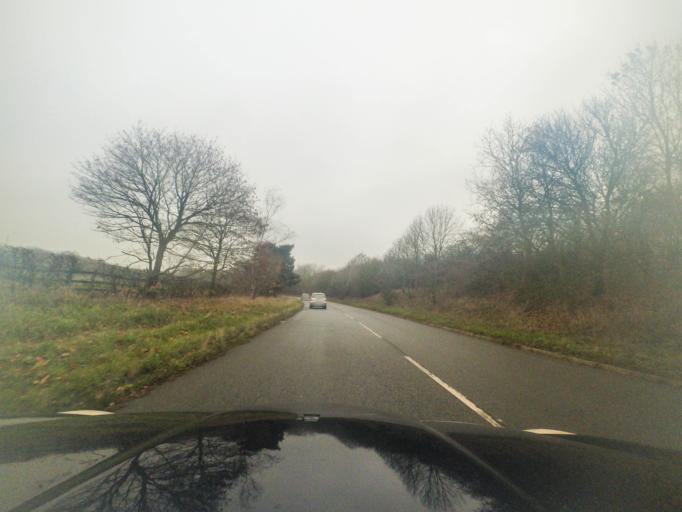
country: GB
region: England
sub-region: Solihull
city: Barston
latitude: 52.3929
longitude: -1.6810
